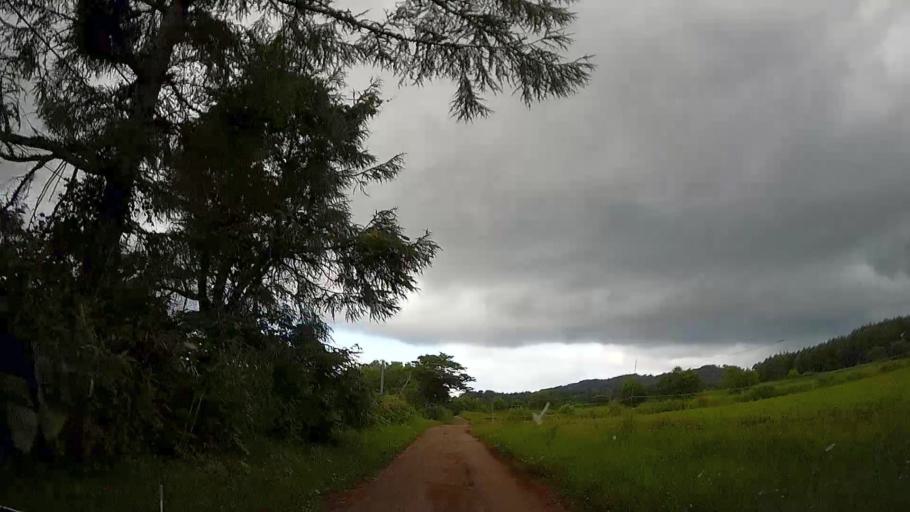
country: JP
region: Hokkaido
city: Nanae
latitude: 42.1240
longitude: 140.4084
